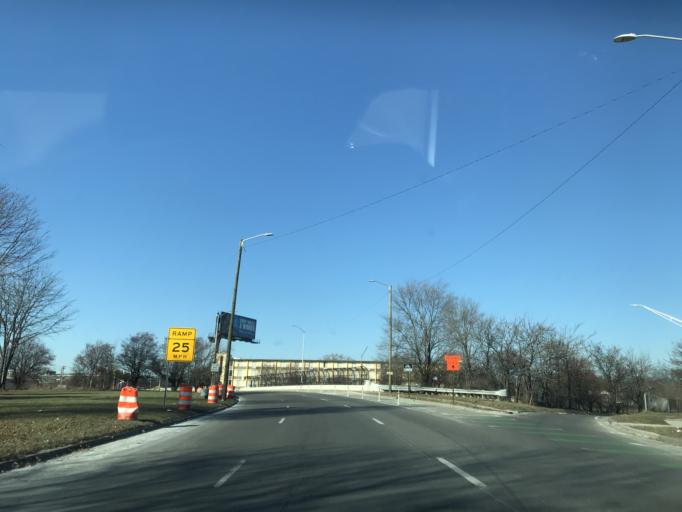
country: US
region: Michigan
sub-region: Wayne County
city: Grosse Pointe Park
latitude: 42.3960
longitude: -82.9869
